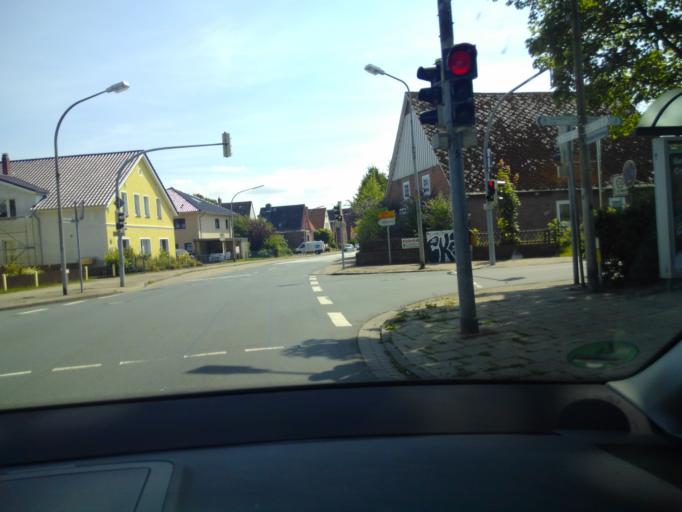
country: DE
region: Lower Saxony
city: Cuxhaven
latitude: 53.8740
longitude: 8.6531
